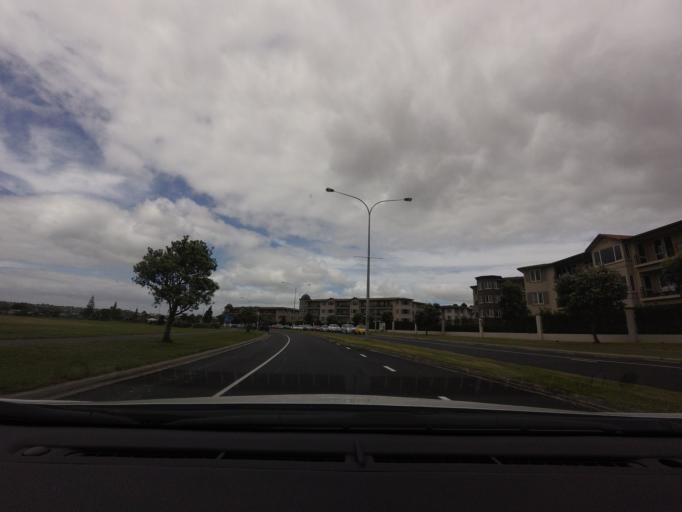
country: NZ
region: Auckland
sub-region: Auckland
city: Rothesay Bay
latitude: -36.5831
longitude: 174.6862
